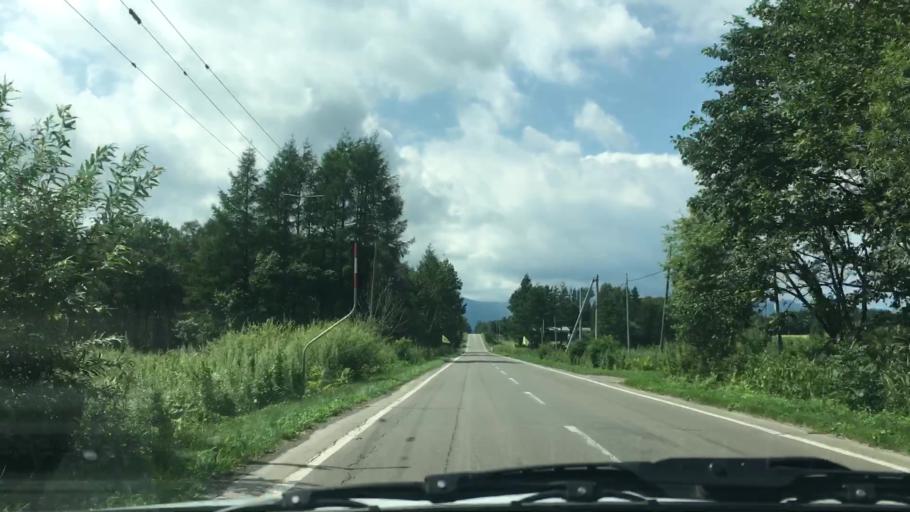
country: JP
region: Hokkaido
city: Otofuke
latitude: 43.2768
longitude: 143.3685
